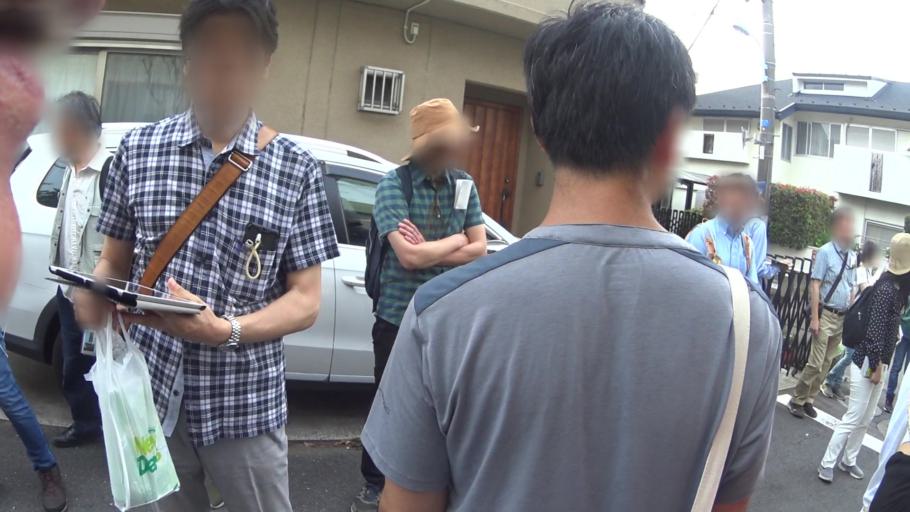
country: JP
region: Tokyo
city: Musashino
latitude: 35.7071
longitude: 139.6254
